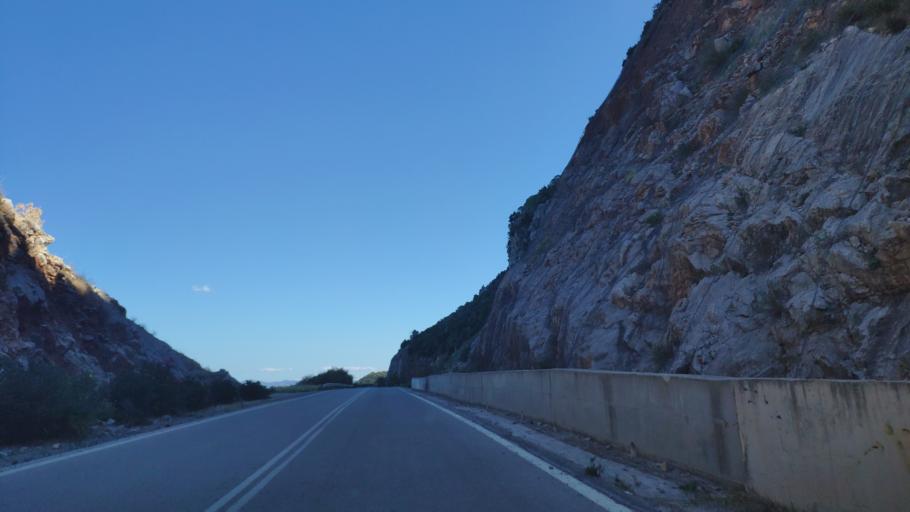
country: GR
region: Peloponnese
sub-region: Nomos Argolidos
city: Palaia Epidavros
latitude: 37.5842
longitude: 23.2286
